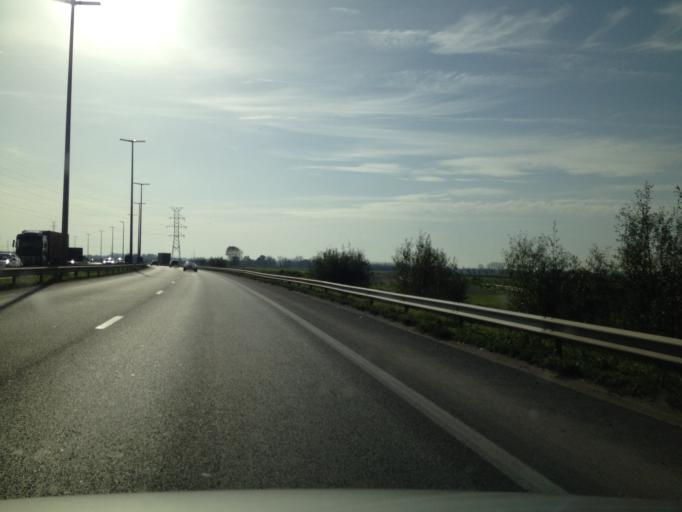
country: BE
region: Flanders
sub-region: Provincie West-Vlaanderen
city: Zuienkerke
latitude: 51.2479
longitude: 3.1855
